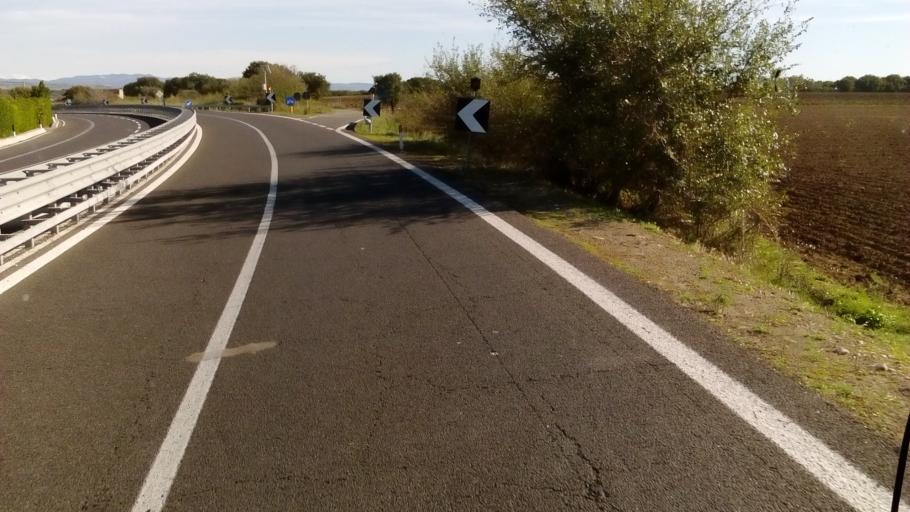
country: IT
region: Latium
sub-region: Provincia di Viterbo
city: Montalto di Castro
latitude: 42.3268
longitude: 11.6331
